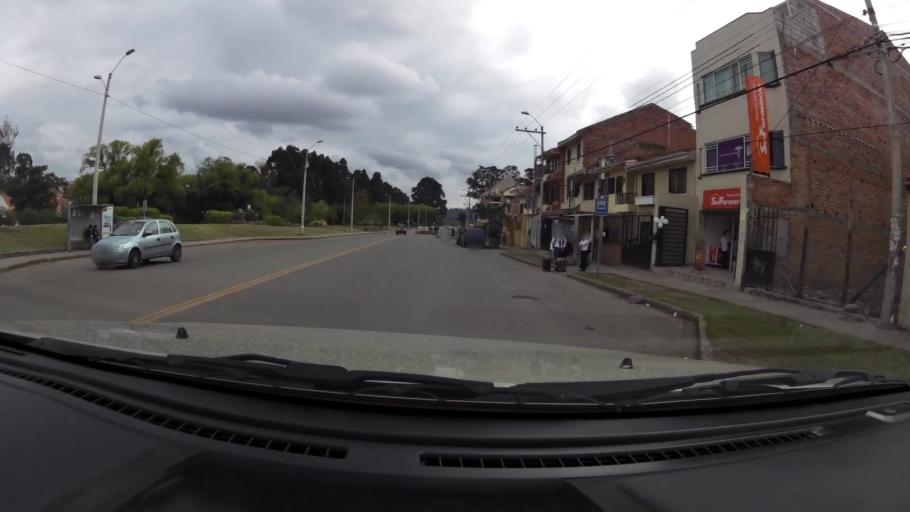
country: EC
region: Azuay
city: Cuenca
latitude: -2.8989
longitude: -78.9741
